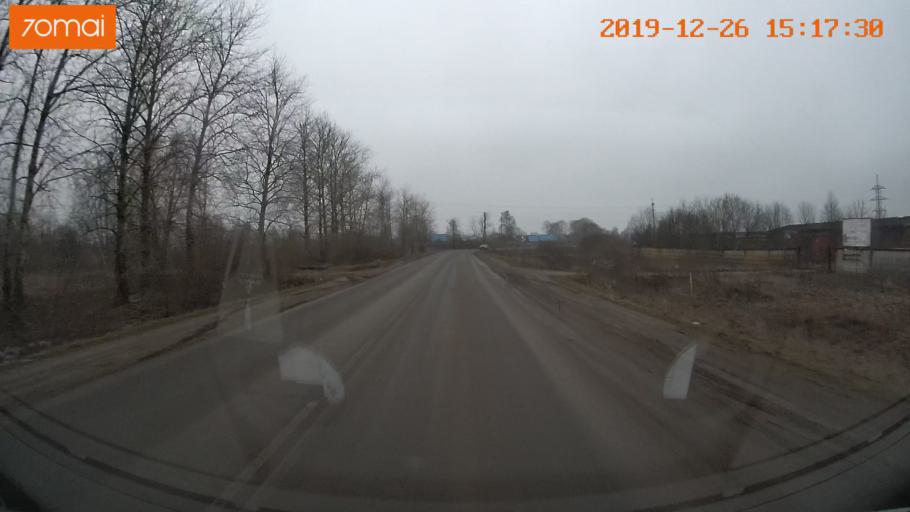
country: RU
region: Jaroslavl
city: Rybinsk
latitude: 58.0765
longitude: 38.8509
